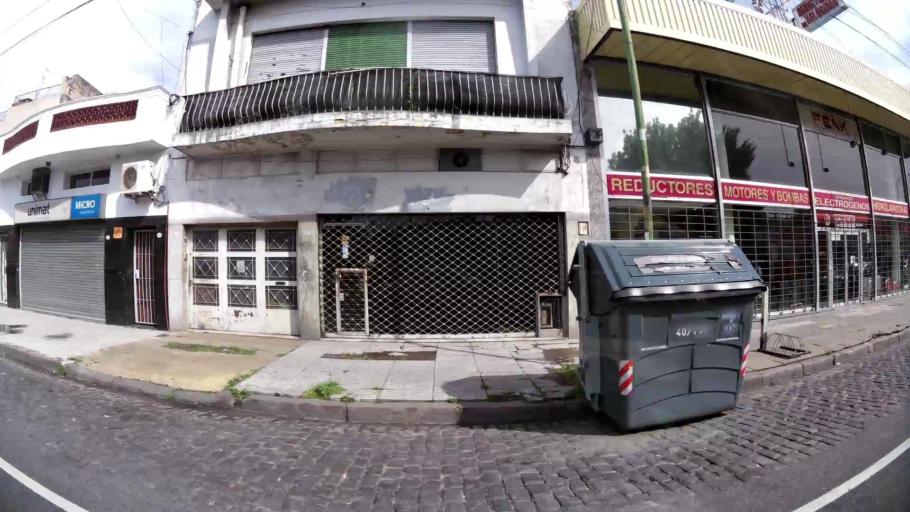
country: AR
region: Buenos Aires F.D.
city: Villa Lugano
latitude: -34.6598
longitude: -58.5136
